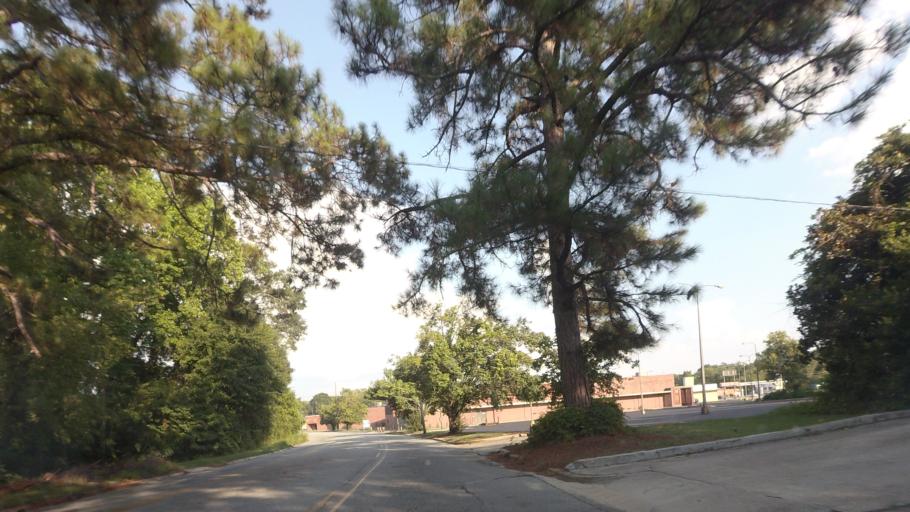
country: US
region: Georgia
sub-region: Bibb County
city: Macon
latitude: 32.8395
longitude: -83.6774
